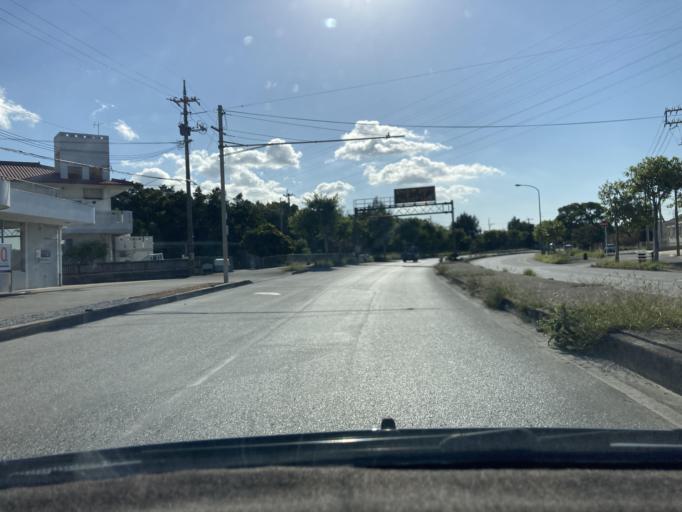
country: JP
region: Okinawa
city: Ishikawa
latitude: 26.4358
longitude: 127.8411
